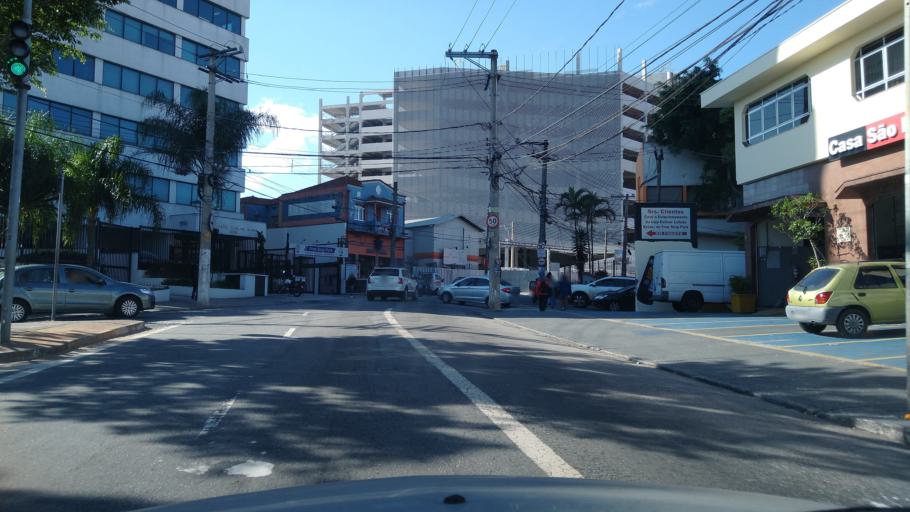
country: BR
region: Sao Paulo
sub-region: Sao Paulo
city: Sao Paulo
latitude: -23.4801
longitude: -46.6112
